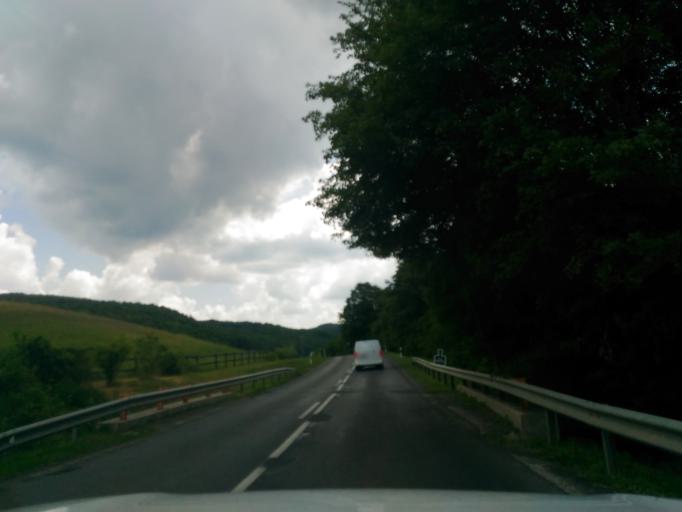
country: HU
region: Baranya
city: Komlo
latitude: 46.1727
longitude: 18.2119
